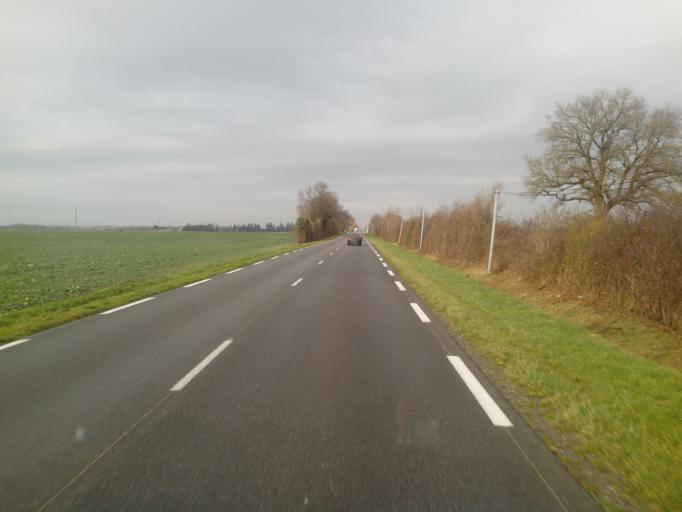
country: FR
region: Poitou-Charentes
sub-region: Departement de la Vienne
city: Saulge
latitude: 46.3079
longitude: 0.8317
